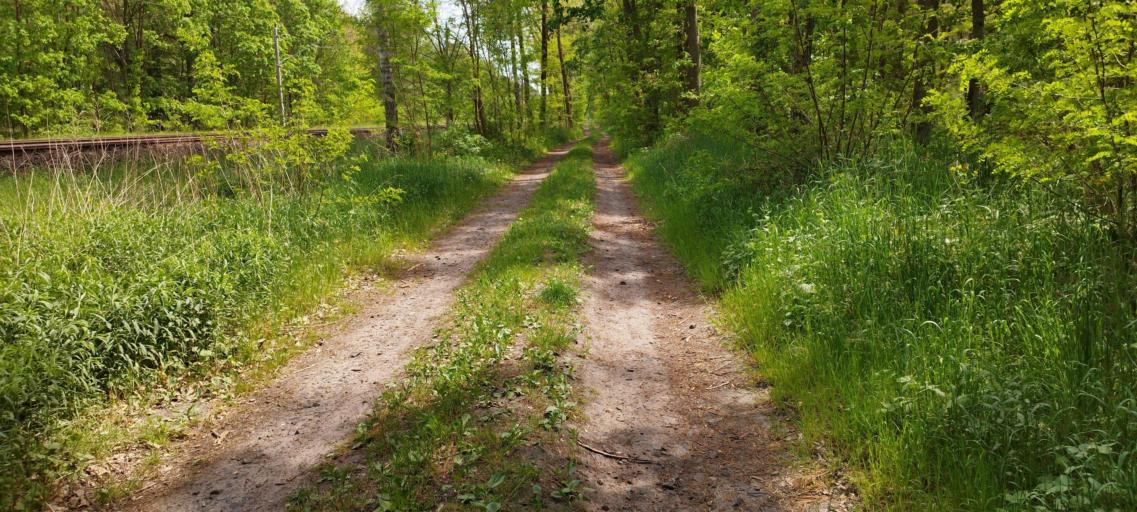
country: DE
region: Brandenburg
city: Spreenhagen
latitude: 52.3908
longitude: 13.9601
